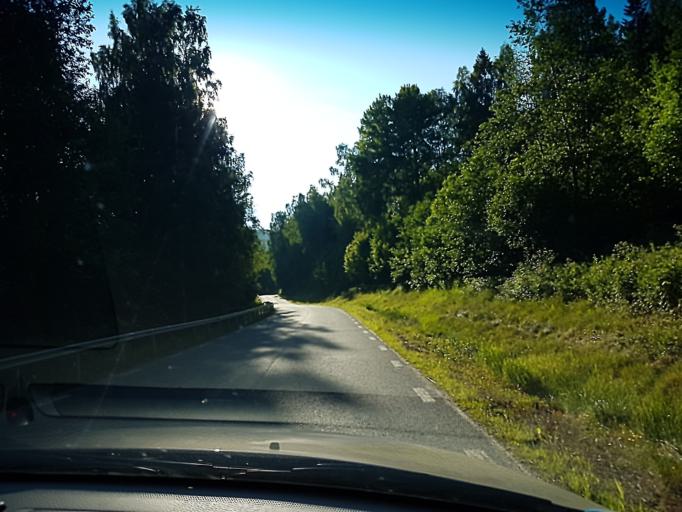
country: SE
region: Vaesternorrland
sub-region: Kramfors Kommun
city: Nordingra
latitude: 63.0640
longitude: 18.3800
